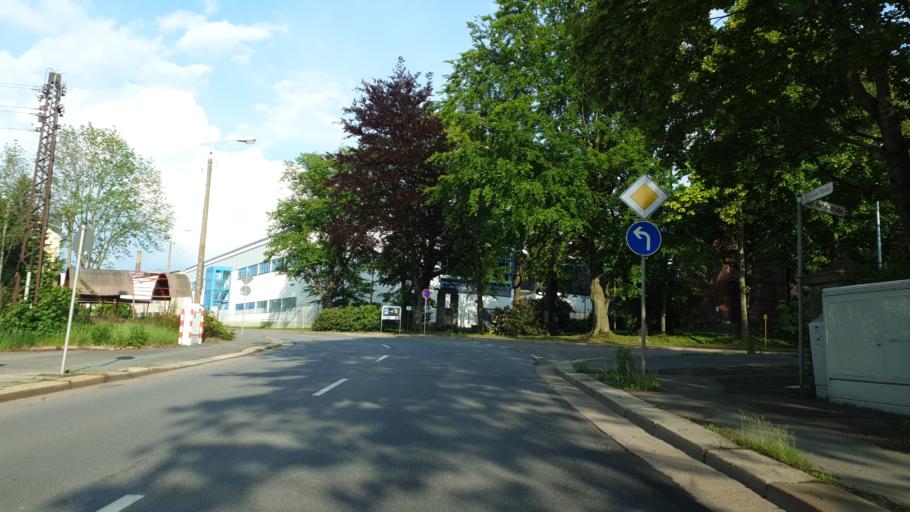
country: DE
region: Saxony
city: Neukirchen
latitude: 50.8193
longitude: 12.8741
